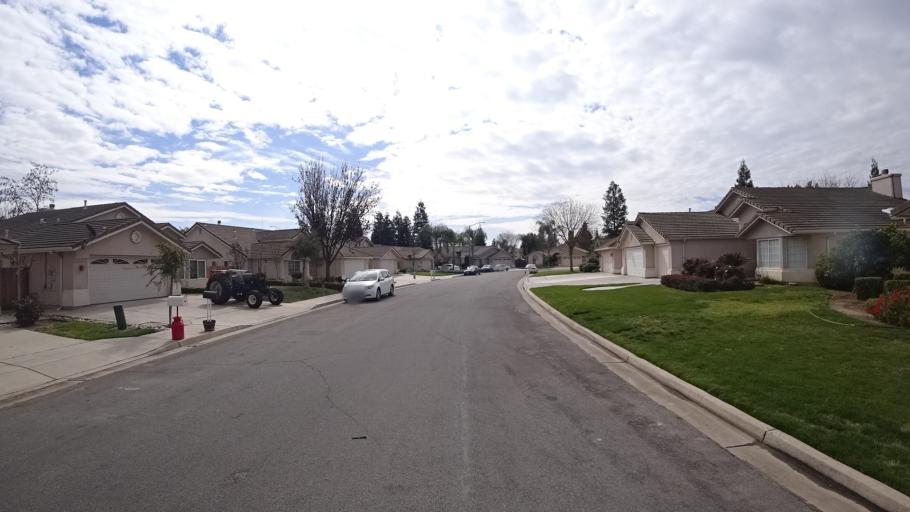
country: US
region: California
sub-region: Fresno County
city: West Park
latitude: 36.8454
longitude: -119.8820
